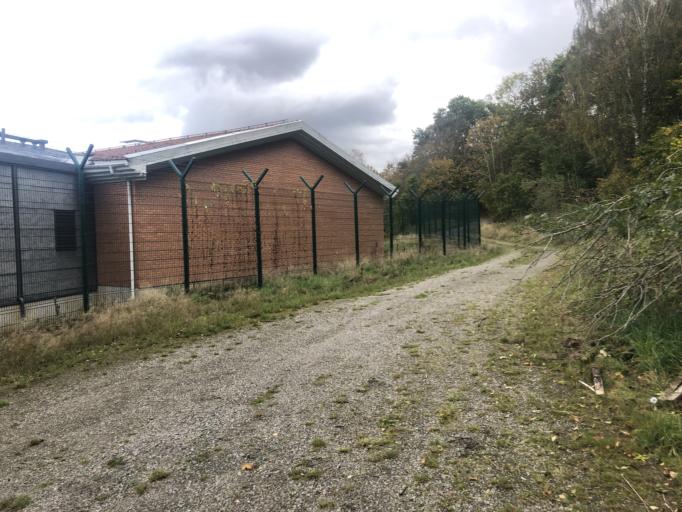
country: SE
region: Vaestra Goetaland
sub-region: Molndal
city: Moelndal
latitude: 57.6405
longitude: 11.9926
